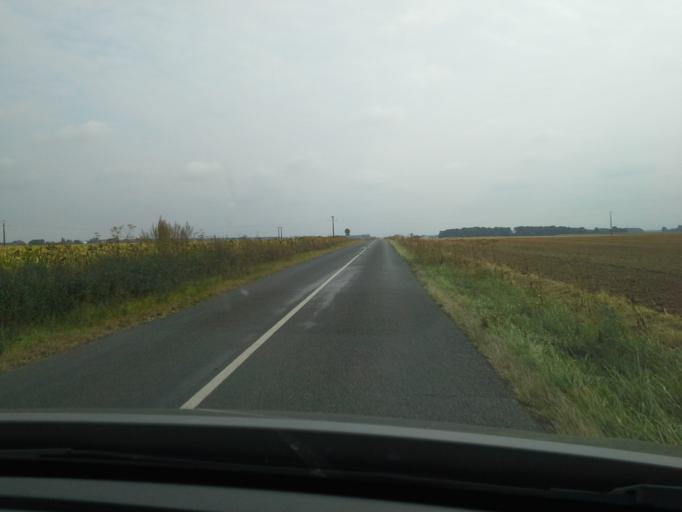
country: FR
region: Centre
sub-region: Departement du Loir-et-Cher
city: Vendome
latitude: 47.7241
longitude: 1.0916
